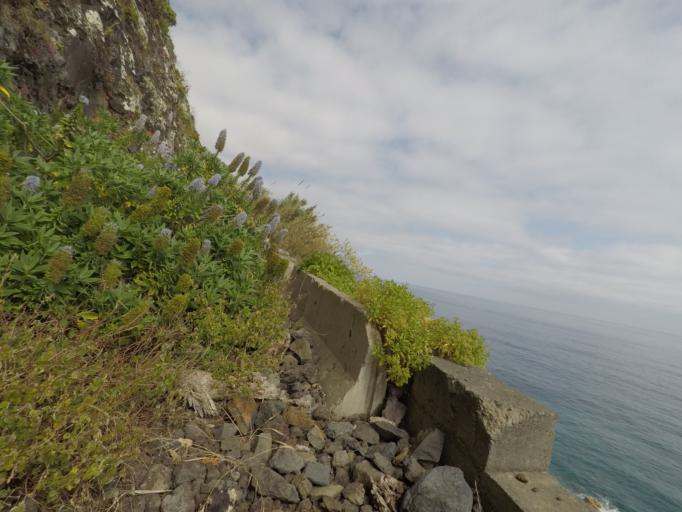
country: PT
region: Madeira
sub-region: Sao Vicente
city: Sao Vicente
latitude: 32.8159
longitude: -17.0835
